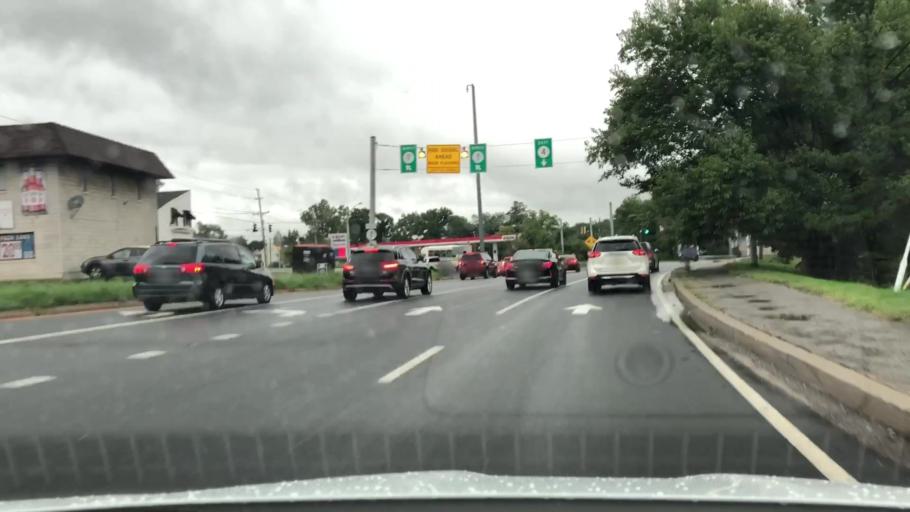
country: US
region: Delaware
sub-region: New Castle County
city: Newport
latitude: 39.7117
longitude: -75.6492
